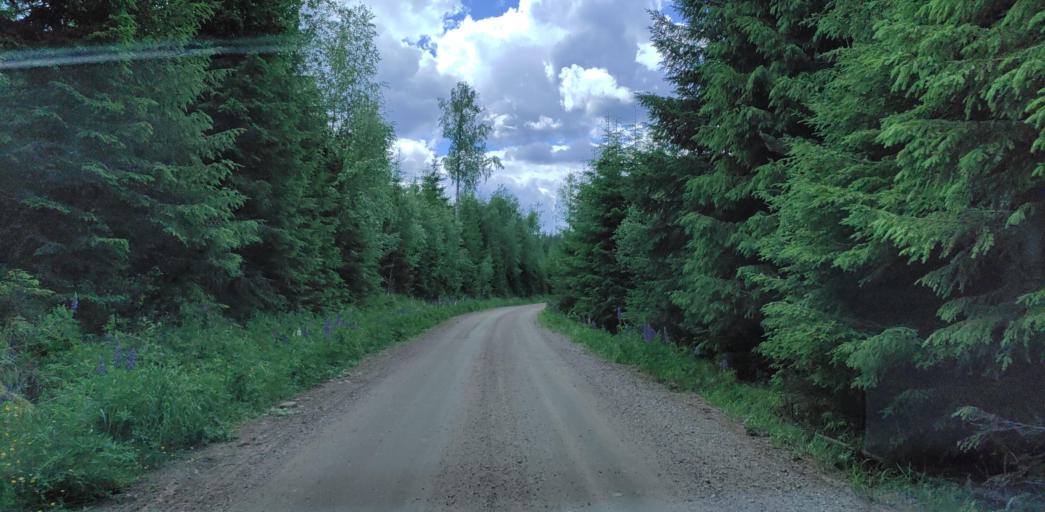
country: SE
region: Vaermland
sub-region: Hagfors Kommun
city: Ekshaerad
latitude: 60.0925
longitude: 13.3428
